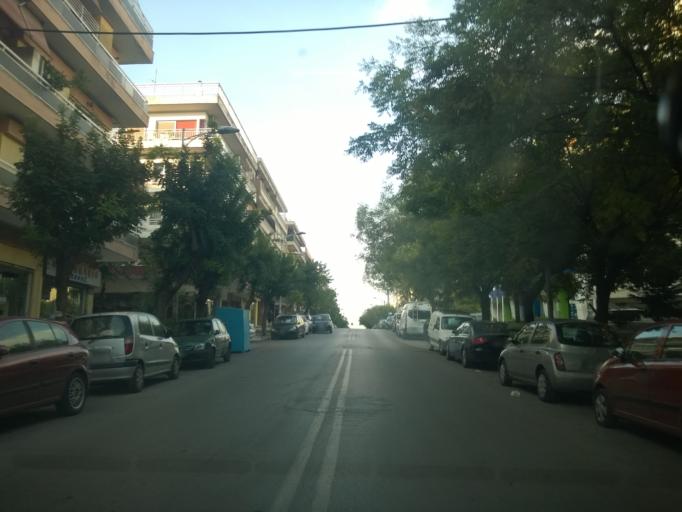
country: GR
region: Central Macedonia
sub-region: Nomos Thessalonikis
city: Kalamaria
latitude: 40.5909
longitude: 22.9619
